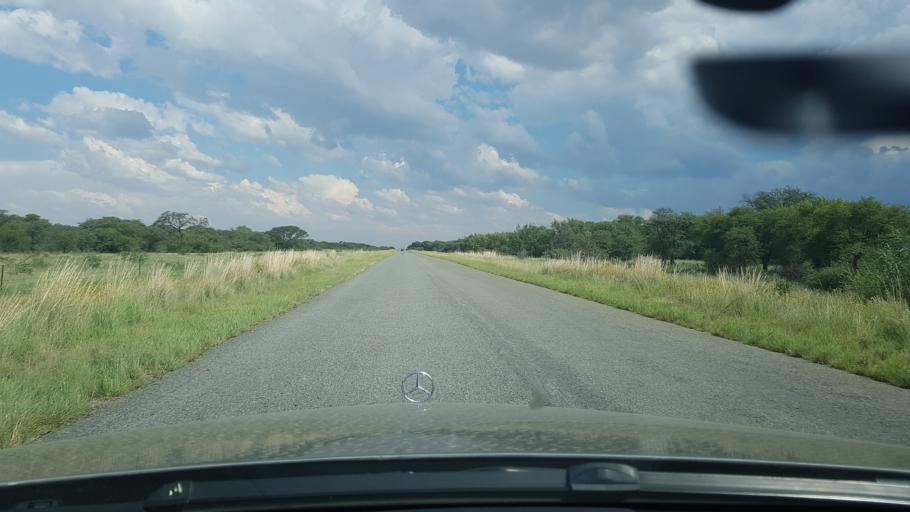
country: ZA
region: North-West
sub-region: Dr Ruth Segomotsi Mompati District Municipality
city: Bloemhof
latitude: -27.7988
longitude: 25.6189
